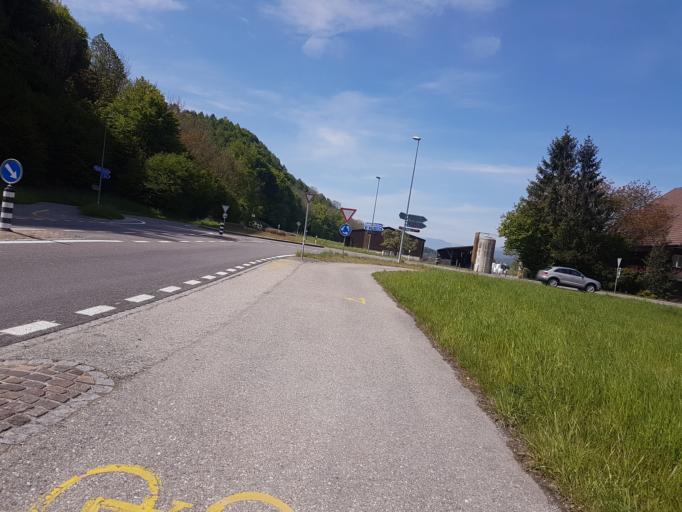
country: CH
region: Neuchatel
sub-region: Neuchatel District
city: Le Landeron
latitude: 47.0402
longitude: 7.0734
